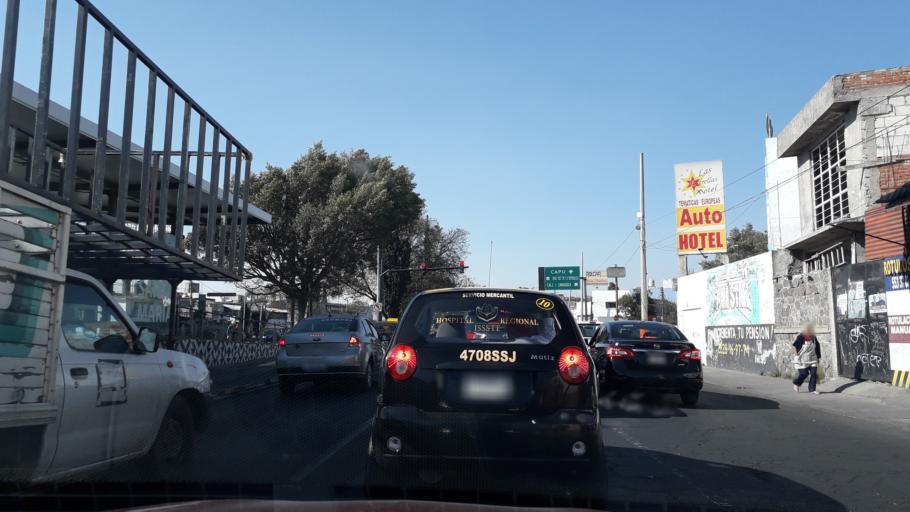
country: MX
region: Puebla
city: Puebla
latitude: 19.0603
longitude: -98.1922
